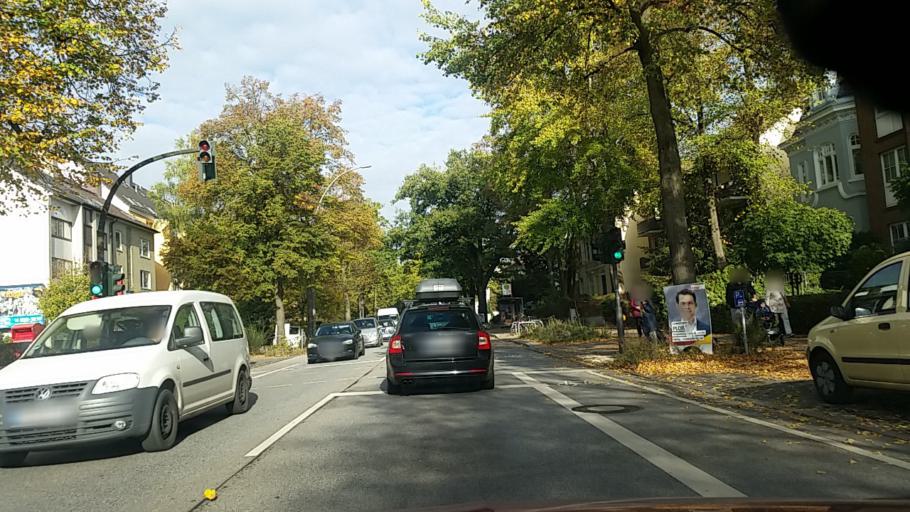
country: DE
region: Hamburg
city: Barmbek-Nord
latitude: 53.6116
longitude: 10.0370
